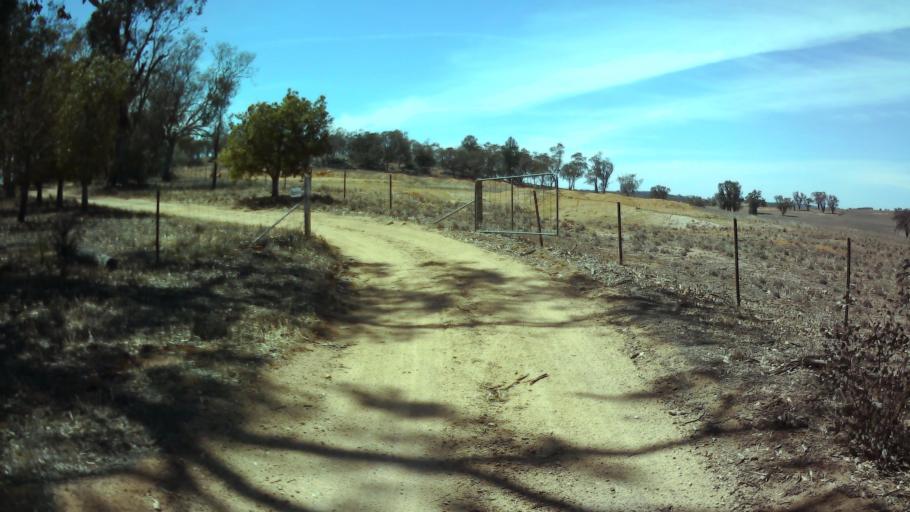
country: AU
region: New South Wales
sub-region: Weddin
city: Grenfell
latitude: -33.9165
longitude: 148.1492
